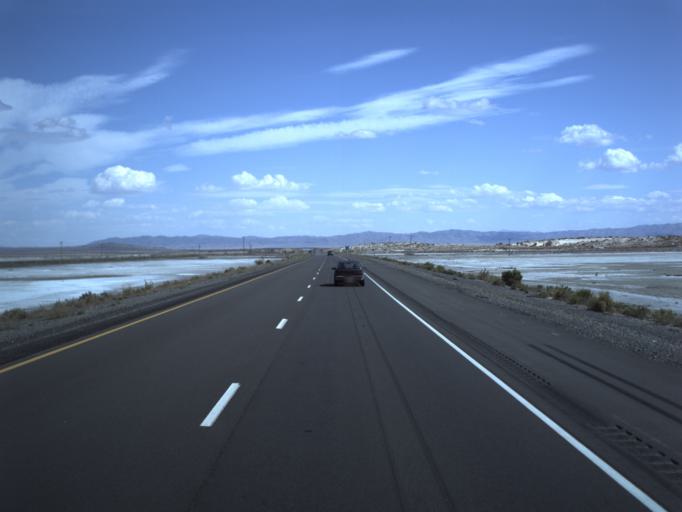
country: US
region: Utah
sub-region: Tooele County
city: Wendover
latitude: 40.7269
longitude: -113.2907
